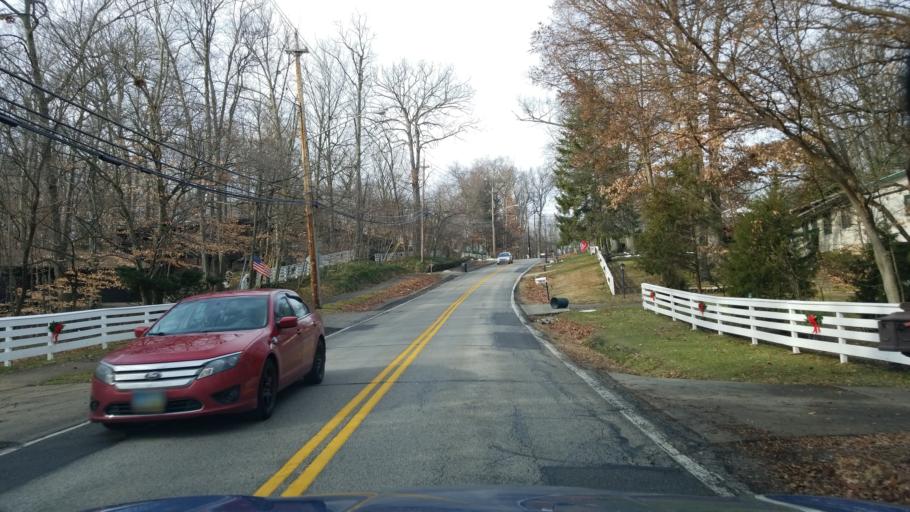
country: US
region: Ohio
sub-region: Cuyahoga County
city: Strongsville
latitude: 41.3330
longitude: -81.8420
